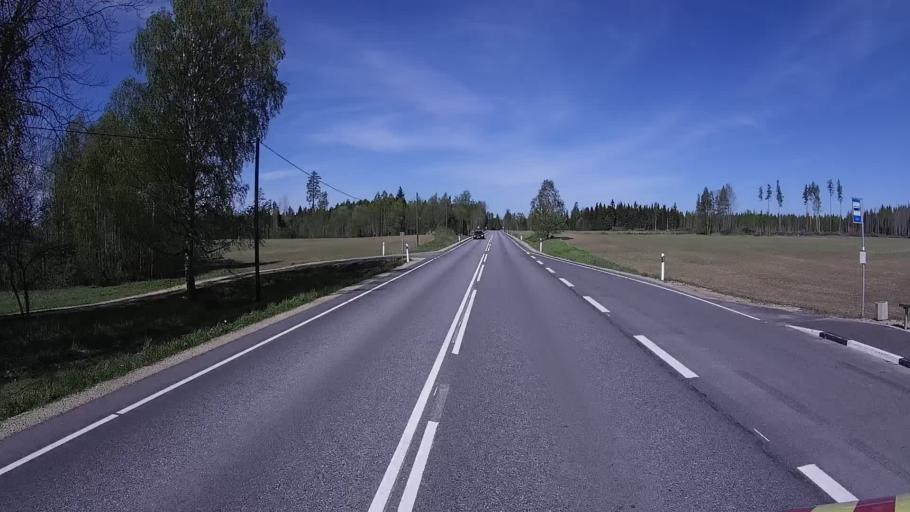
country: EE
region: Polvamaa
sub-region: Raepina vald
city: Rapina
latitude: 57.9783
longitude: 27.2878
